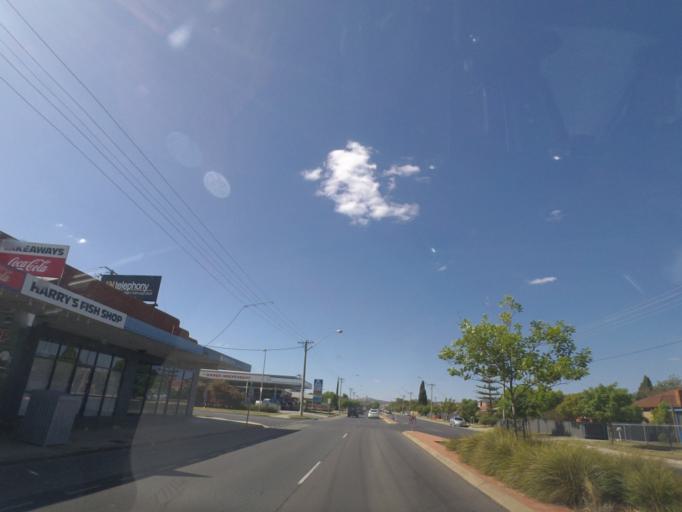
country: AU
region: New South Wales
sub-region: Albury Municipality
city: North Albury
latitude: -36.0581
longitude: 146.9325
